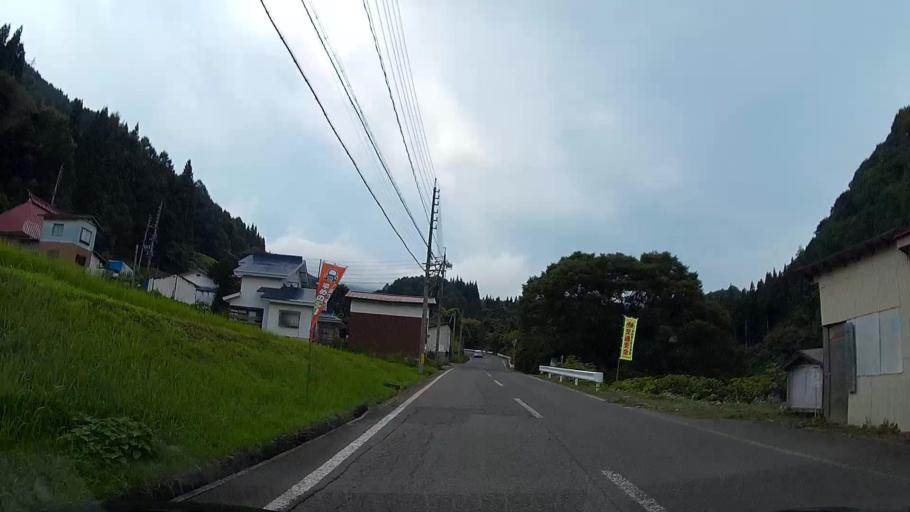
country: JP
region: Nagano
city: Iiyama
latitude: 36.8237
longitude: 138.4313
